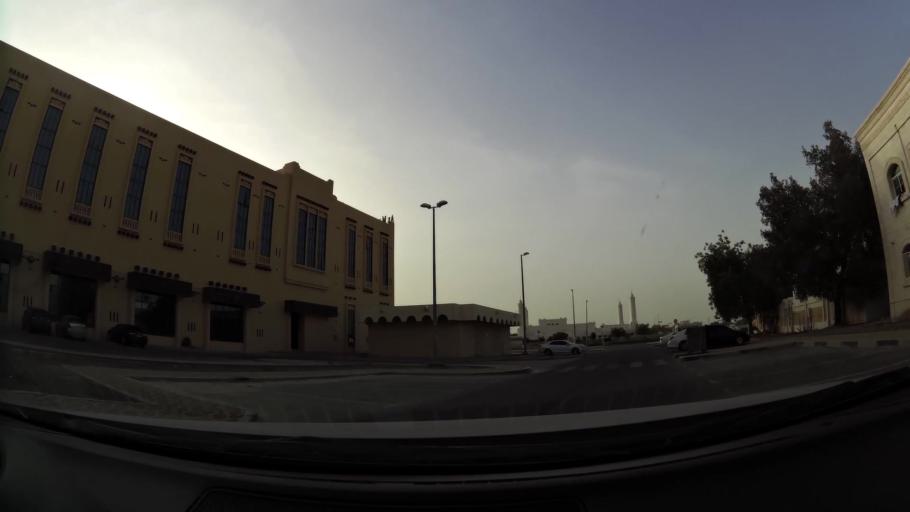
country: OM
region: Al Buraimi
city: Al Buraymi
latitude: 24.2420
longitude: 55.7406
